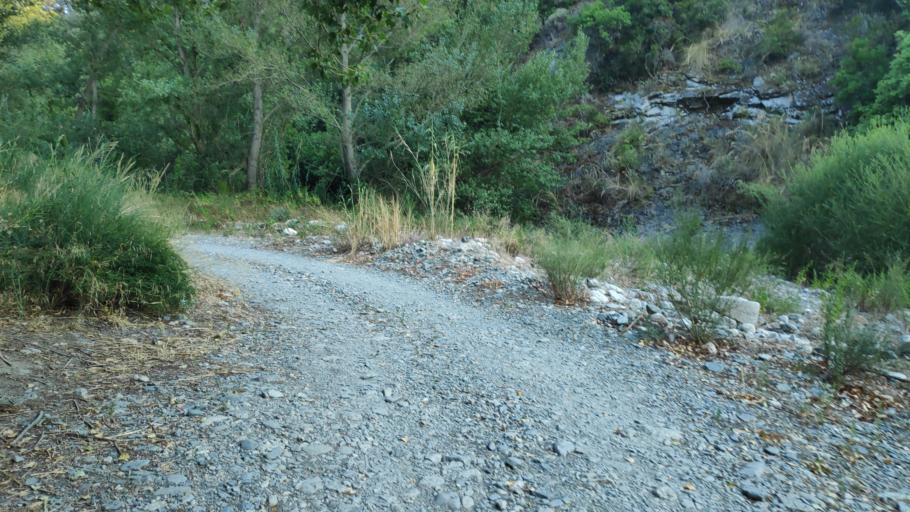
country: IT
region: Calabria
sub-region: Provincia di Reggio Calabria
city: Placanica
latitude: 38.4141
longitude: 16.4375
